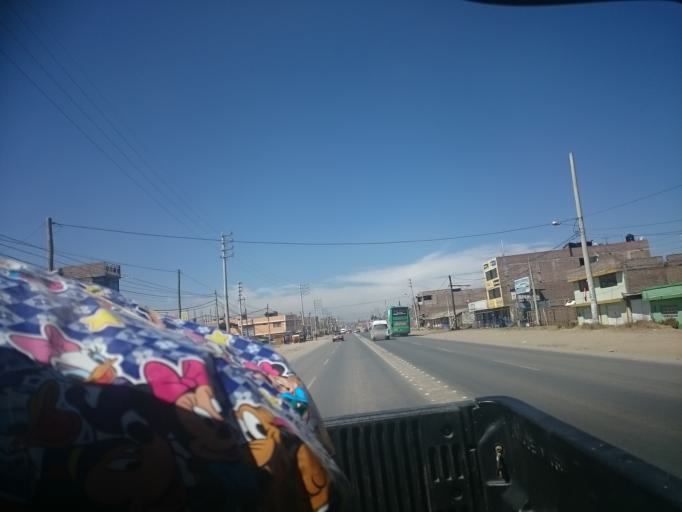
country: PE
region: Junin
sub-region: Provincia de Huancayo
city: San Agustin
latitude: -12.0004
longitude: -75.2523
